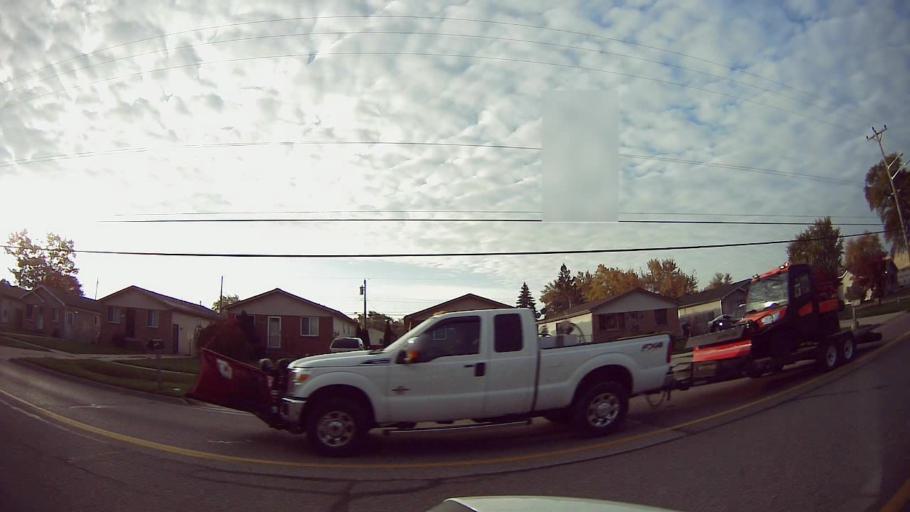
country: US
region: Michigan
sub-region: Macomb County
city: Fraser
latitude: 42.5394
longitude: -82.9158
